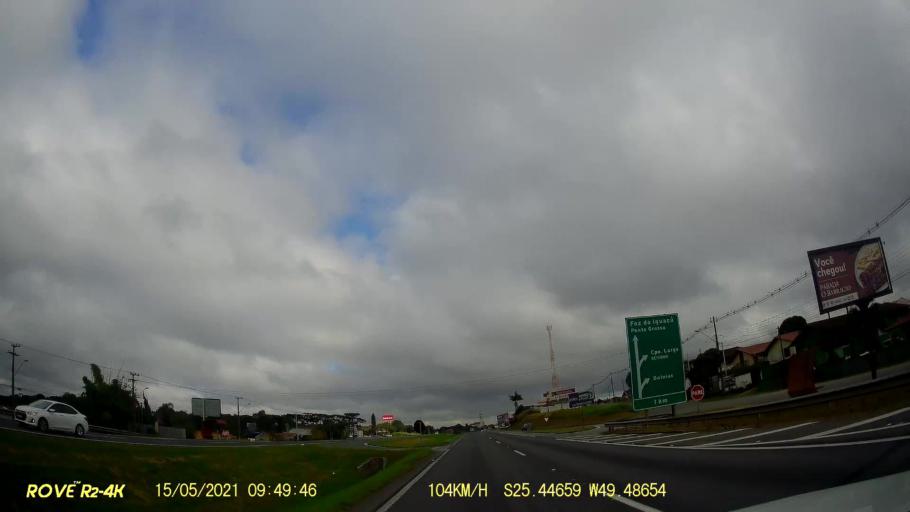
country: BR
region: Parana
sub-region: Campo Largo
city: Campo Largo
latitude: -25.4466
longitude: -49.4865
